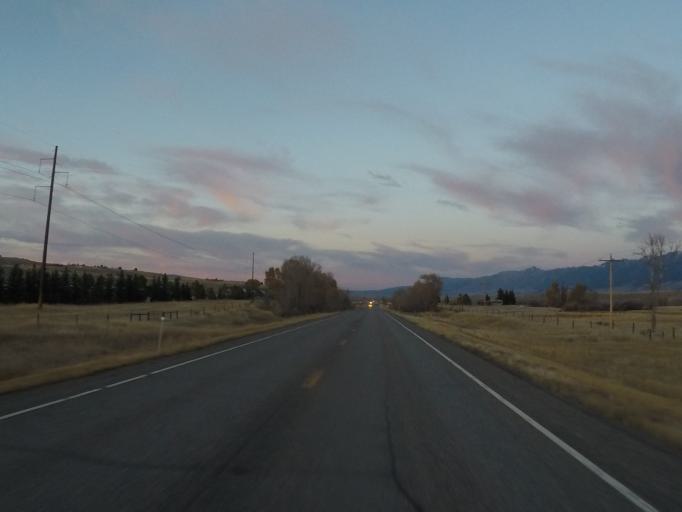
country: US
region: Montana
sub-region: Park County
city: Livingston
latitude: 45.3613
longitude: -110.7407
